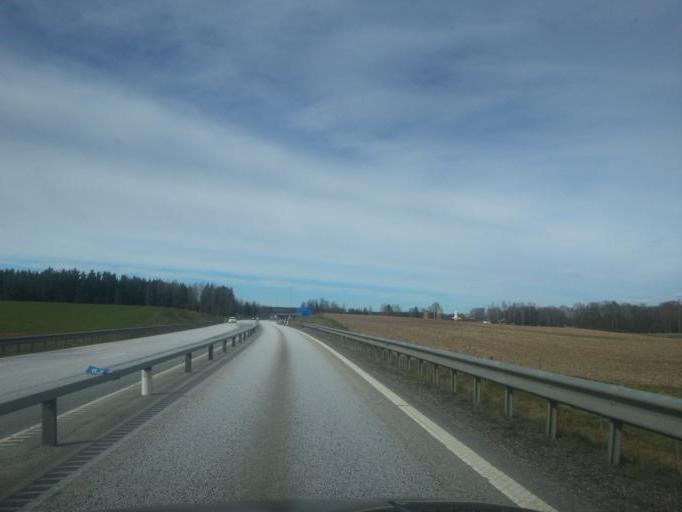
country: SE
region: Joenkoeping
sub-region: Jonkopings Kommun
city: Bankeryd
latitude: 57.8237
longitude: 14.1029
